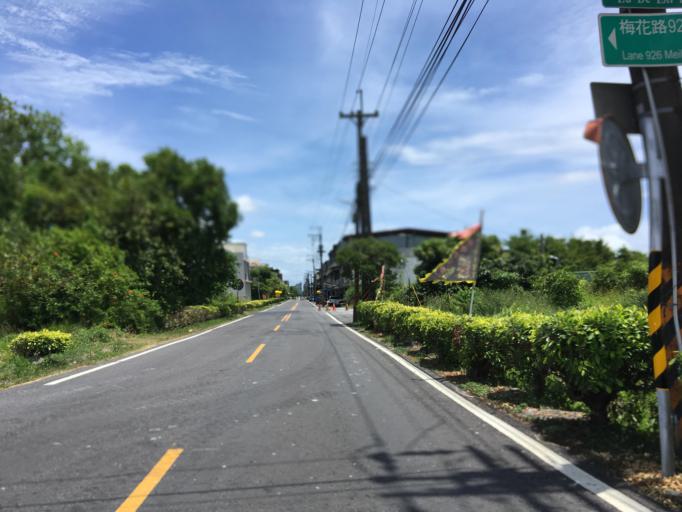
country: TW
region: Taiwan
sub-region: Yilan
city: Yilan
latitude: 24.6568
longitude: 121.7317
